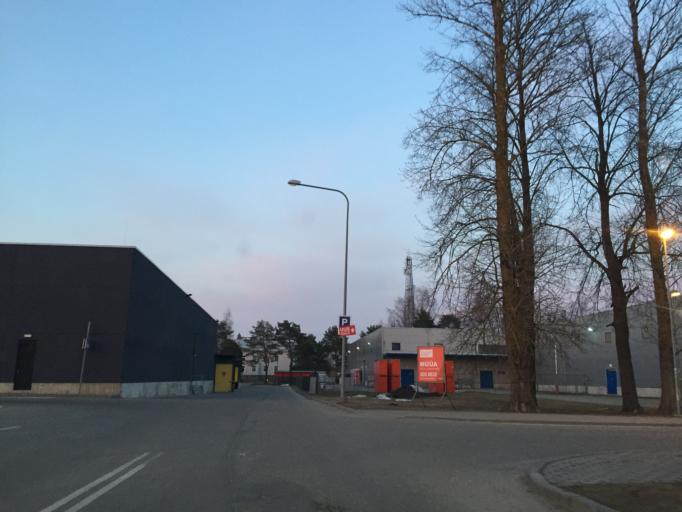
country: EE
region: Paernumaa
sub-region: Paernu linn
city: Parnu
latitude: 58.3689
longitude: 24.5506
